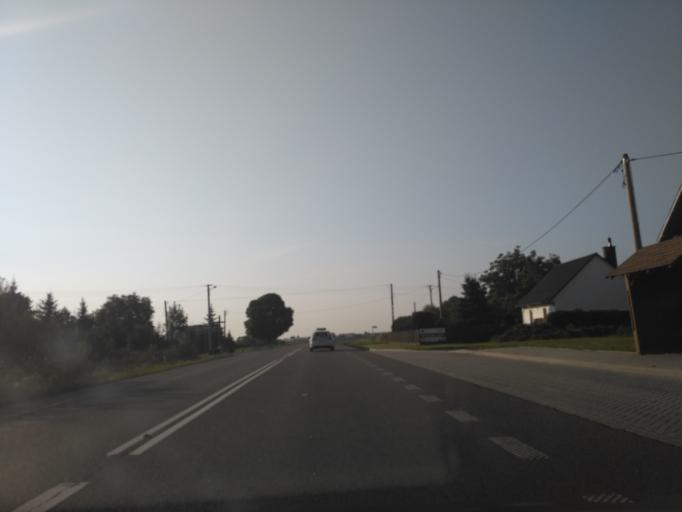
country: PL
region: Lublin Voivodeship
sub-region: Powiat janowski
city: Modliborzyce
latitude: 50.7392
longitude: 22.3492
